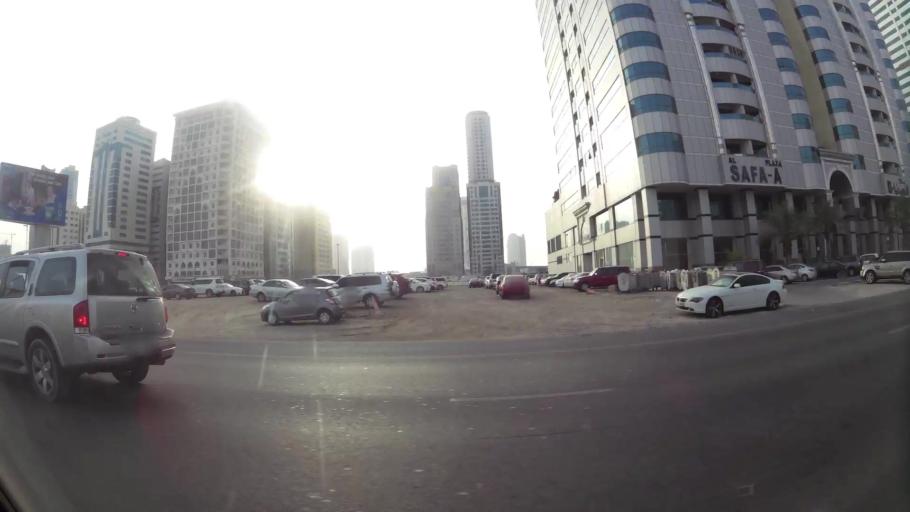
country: AE
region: Ash Shariqah
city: Sharjah
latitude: 25.3079
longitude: 55.3760
